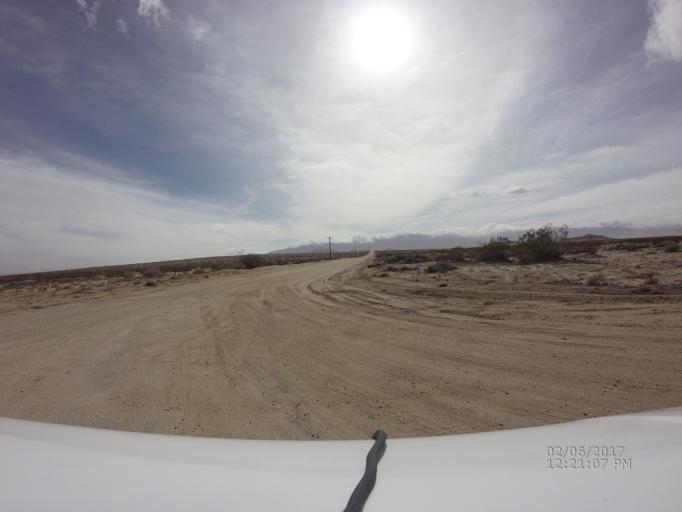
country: US
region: California
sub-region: Los Angeles County
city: Lake Los Angeles
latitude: 34.6164
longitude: -117.7383
